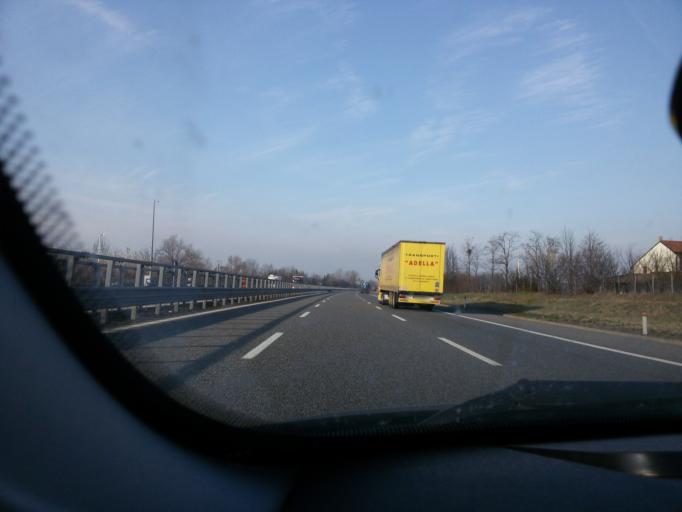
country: IT
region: Piedmont
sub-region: Provincia di Alessandria
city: Mirabello Monferrato
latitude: 45.0134
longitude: 8.5350
